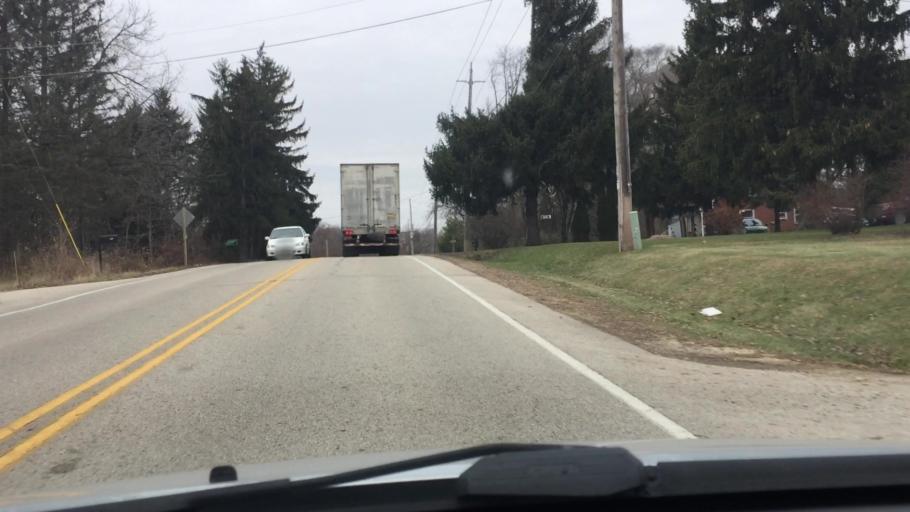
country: US
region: Wisconsin
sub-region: Ozaukee County
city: Grafton
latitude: 43.2999
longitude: -87.9606
